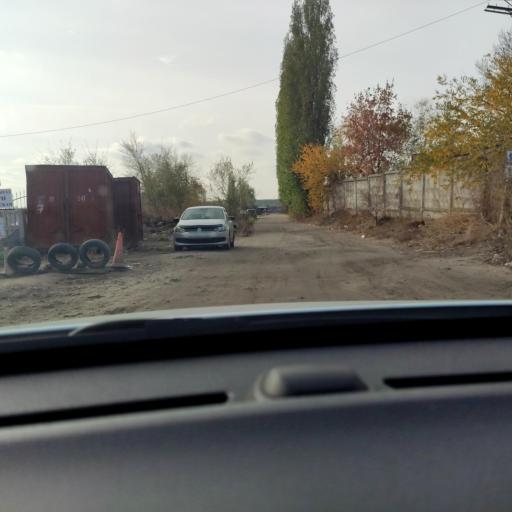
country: RU
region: Voronezj
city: Voronezh
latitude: 51.6383
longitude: 39.1533
